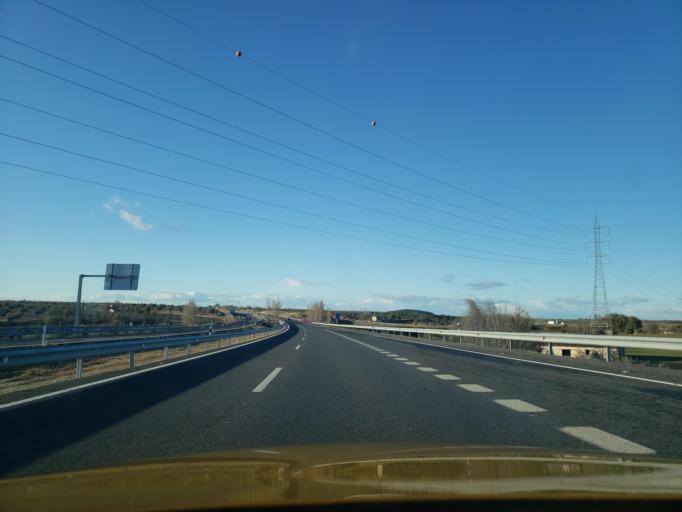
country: ES
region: Castille-La Mancha
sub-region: Province of Toledo
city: Villaminaya
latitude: 39.7589
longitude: -3.8698
